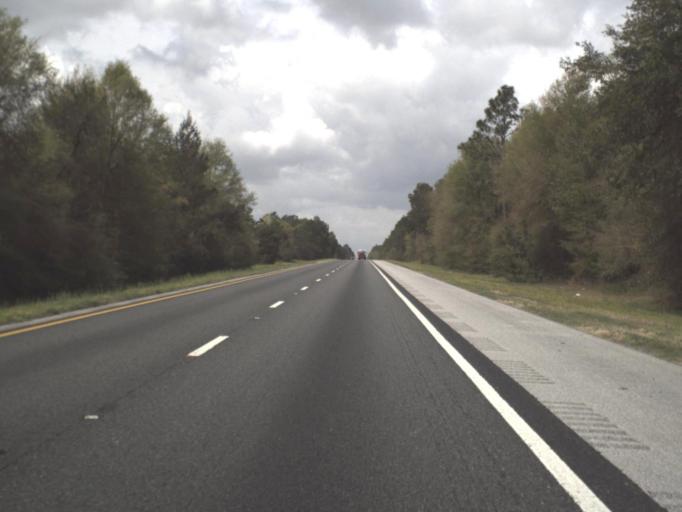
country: US
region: Florida
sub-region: Okaloosa County
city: Crestview
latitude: 30.7120
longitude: -86.7061
